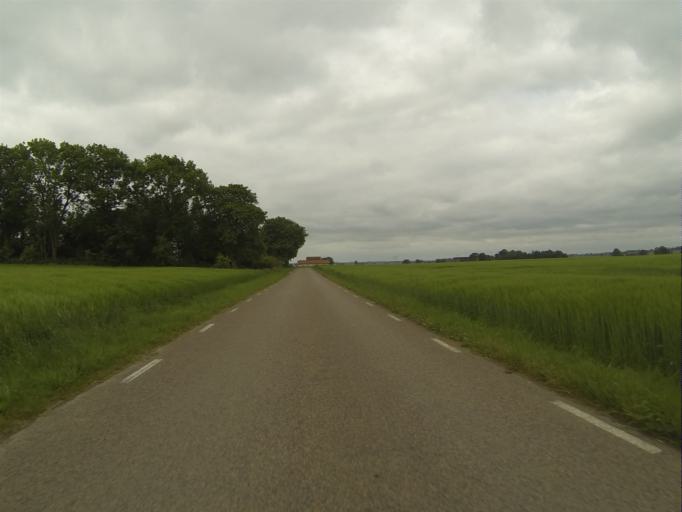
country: SE
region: Skane
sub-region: Staffanstorps Kommun
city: Staffanstorp
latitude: 55.6814
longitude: 13.2666
